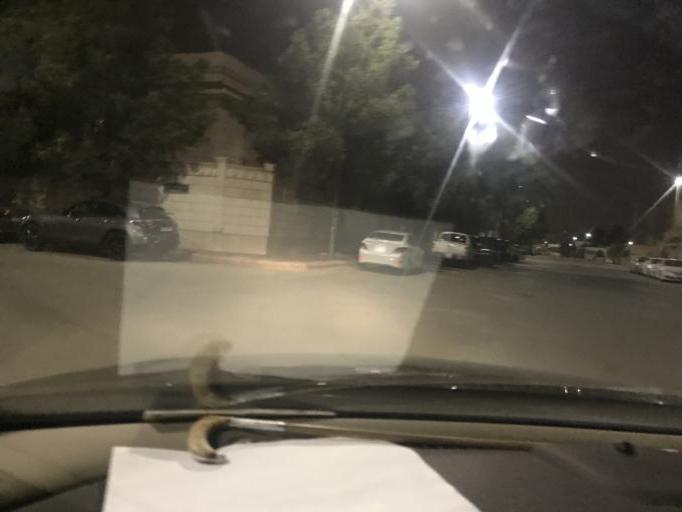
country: SA
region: Ar Riyad
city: Riyadh
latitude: 24.7248
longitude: 46.7732
